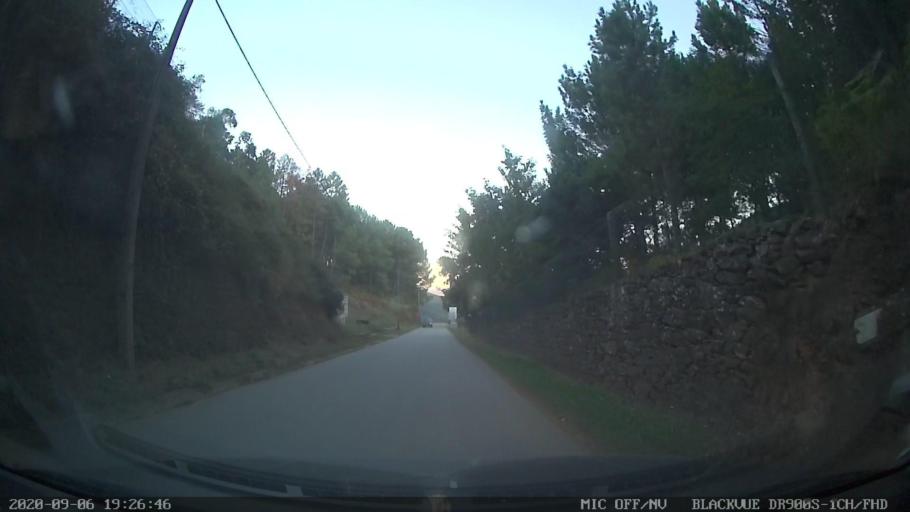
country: PT
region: Vila Real
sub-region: Mesao Frio
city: Mesao Frio
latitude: 41.1806
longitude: -7.9147
